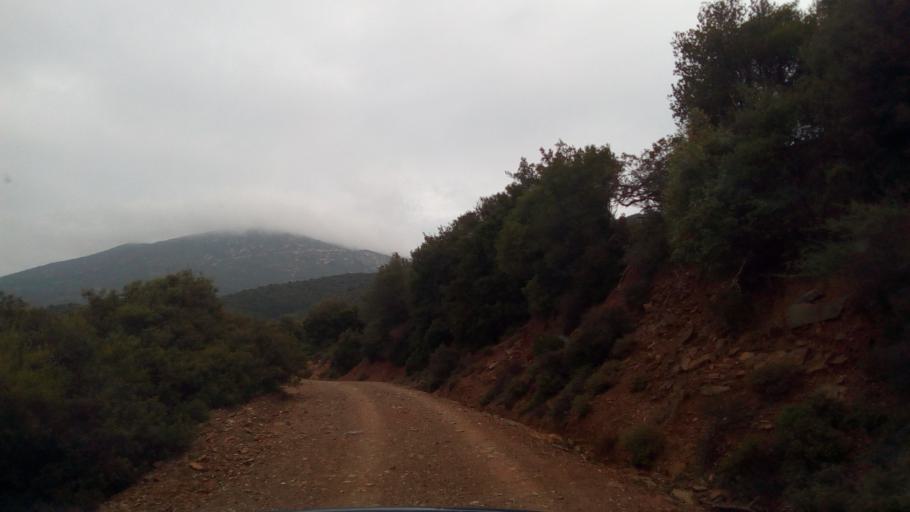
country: GR
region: West Greece
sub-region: Nomos Achaias
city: Temeni
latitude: 38.3650
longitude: 22.1592
